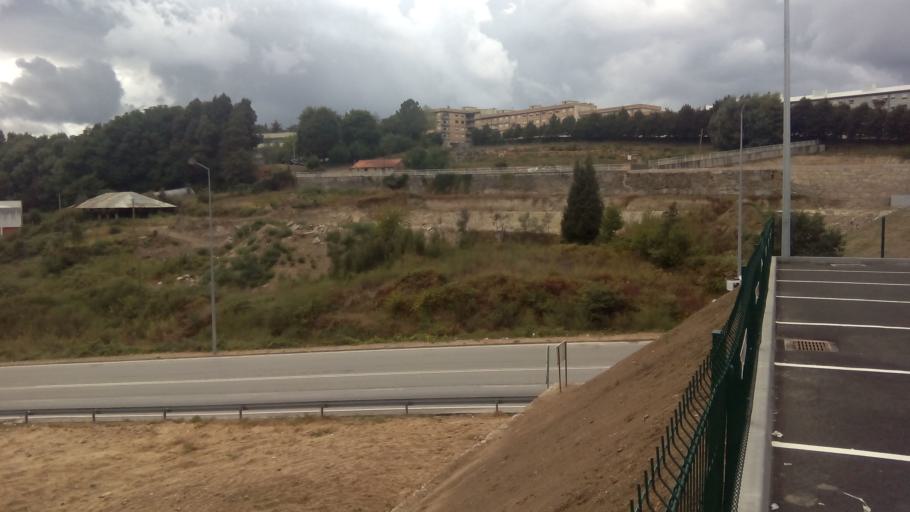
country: PT
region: Porto
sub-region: Penafiel
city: Penafiel
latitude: 41.2101
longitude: -8.2703
